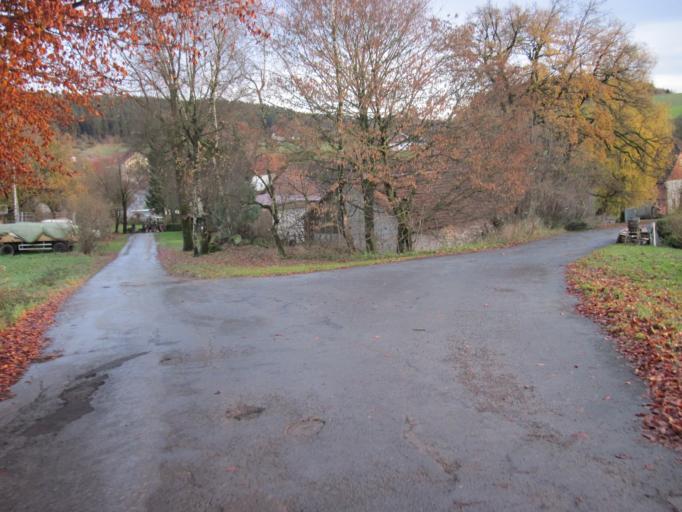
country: DE
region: North Rhine-Westphalia
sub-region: Regierungsbezirk Detmold
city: Altenbeken
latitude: 51.8046
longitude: 8.9420
